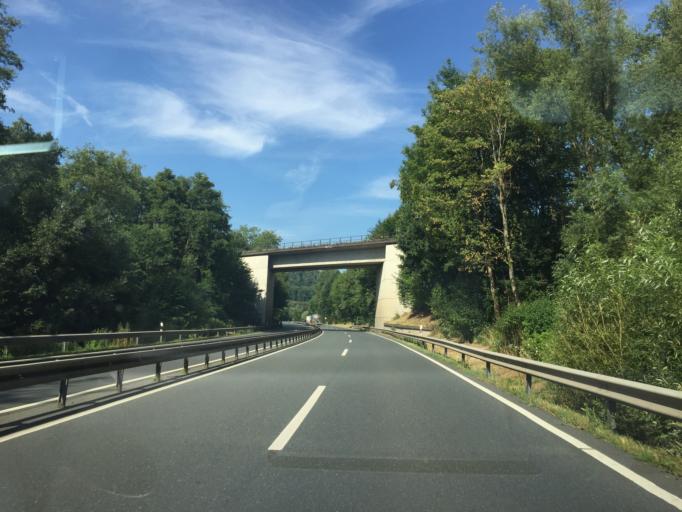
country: DE
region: Lower Saxony
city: Seesen
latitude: 51.8666
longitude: 10.1415
